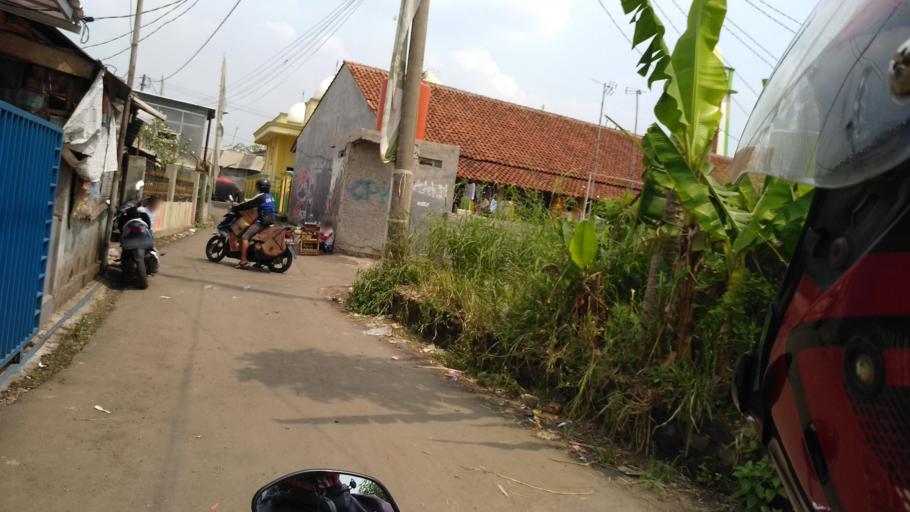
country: ID
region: West Java
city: Ciampea
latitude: -6.5611
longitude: 106.7457
